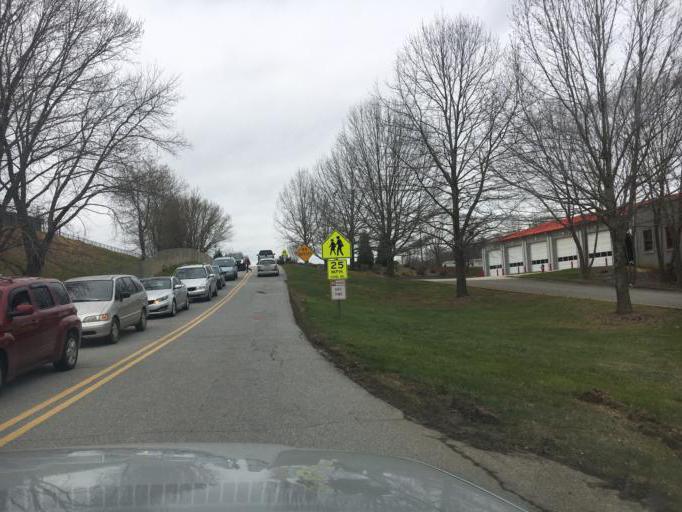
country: US
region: North Carolina
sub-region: Buncombe County
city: Woodfin
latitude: 35.6157
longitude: -82.6303
